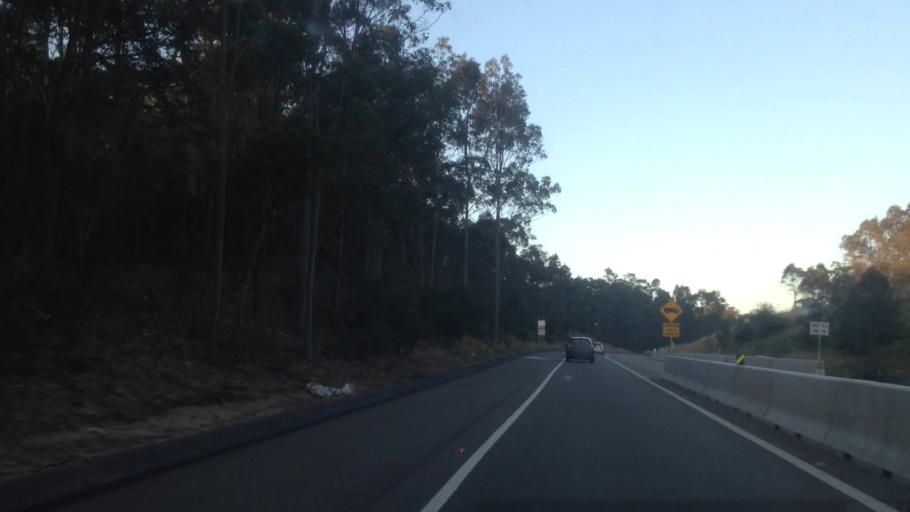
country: AU
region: New South Wales
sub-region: Wyong Shire
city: Jilliby
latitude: -33.2179
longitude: 151.4405
